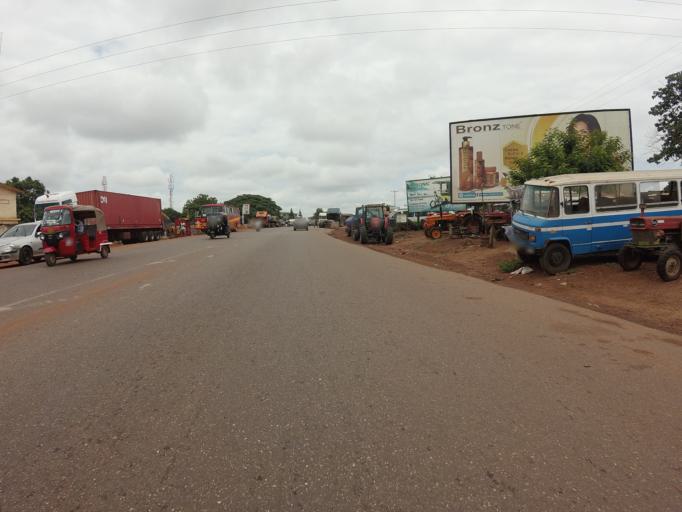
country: GH
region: Brong-Ahafo
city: Techiman
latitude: 7.5951
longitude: -1.9359
